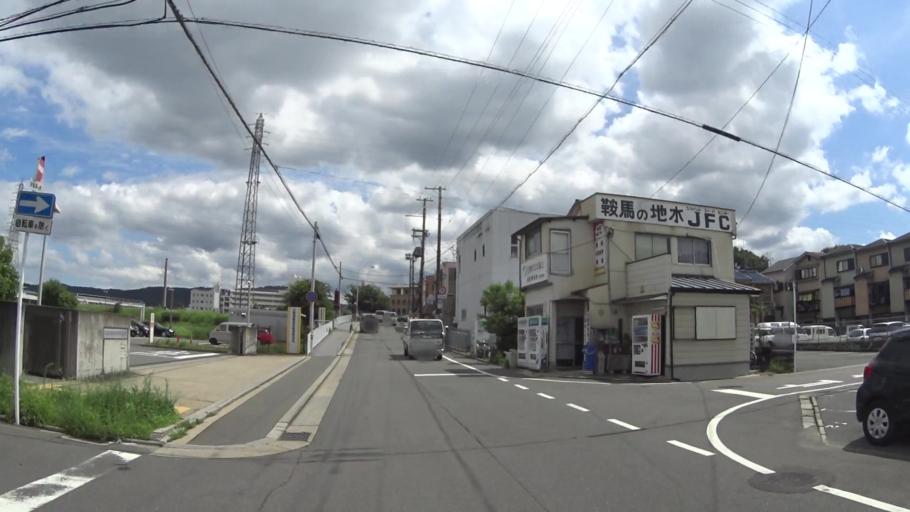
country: JP
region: Kyoto
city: Muko
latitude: 34.9643
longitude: 135.7553
